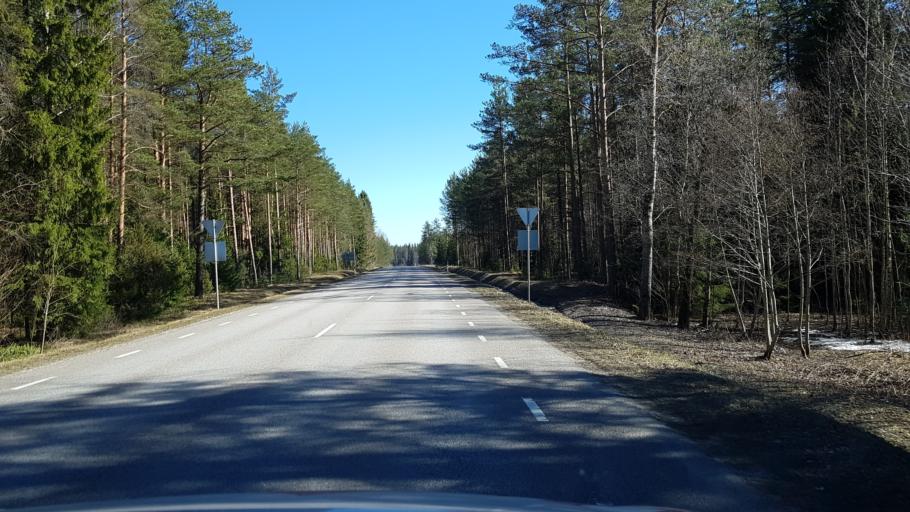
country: EE
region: Laeaene-Virumaa
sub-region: Viru-Nigula vald
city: Kunda
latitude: 59.3736
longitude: 26.5895
